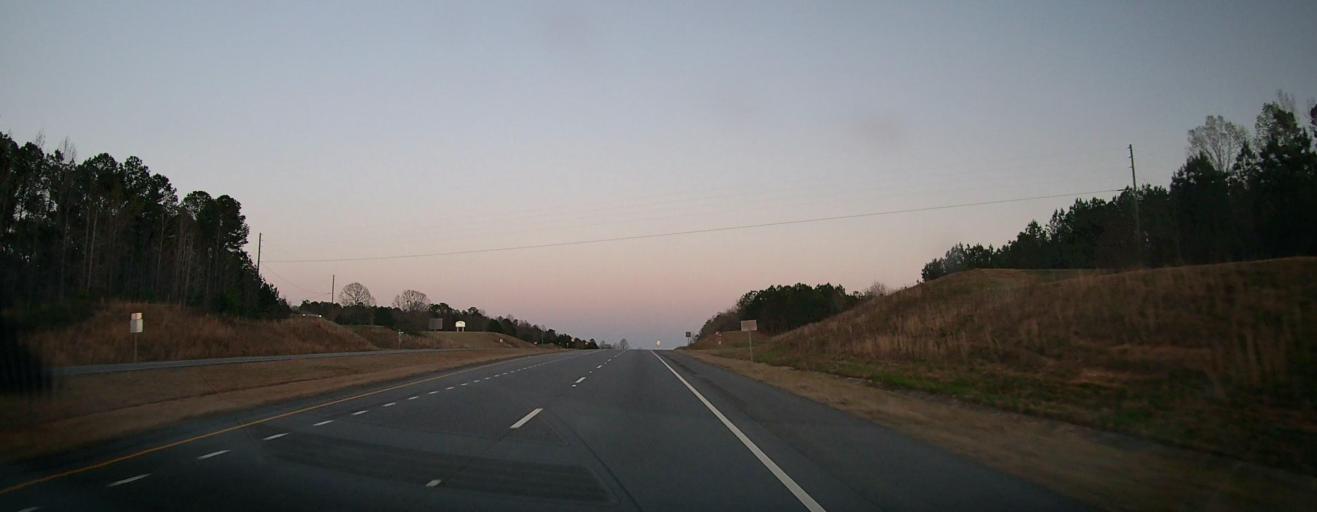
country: US
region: Alabama
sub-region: Tallapoosa County
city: Dadeville
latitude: 32.8794
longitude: -85.8264
